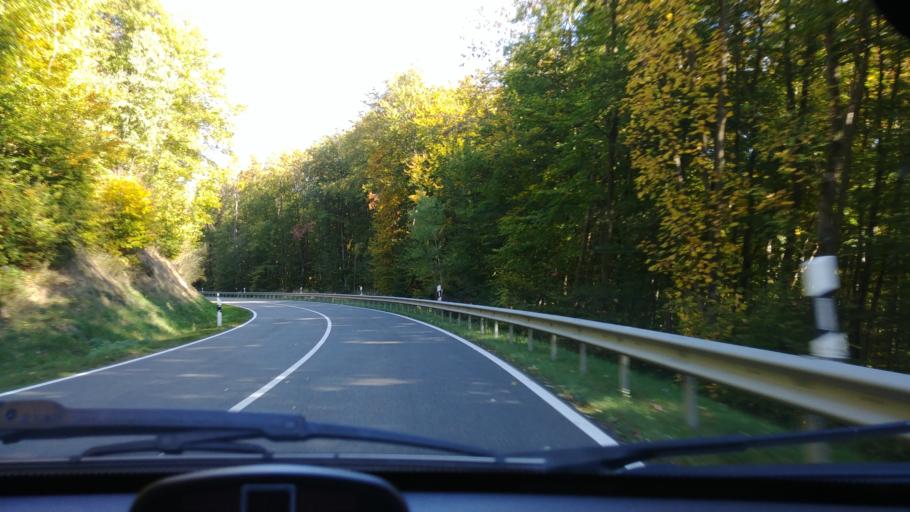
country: DE
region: Rheinland-Pfalz
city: Mudershausen
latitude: 50.2807
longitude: 8.0253
